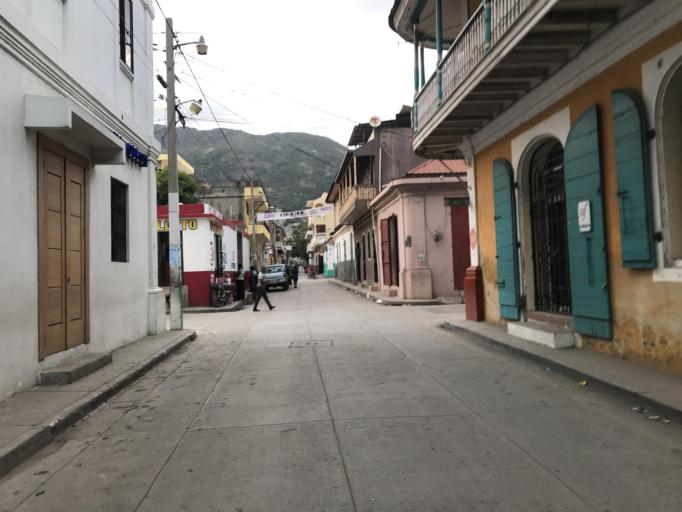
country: HT
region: Nord
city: Okap
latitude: 19.7595
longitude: -72.1999
